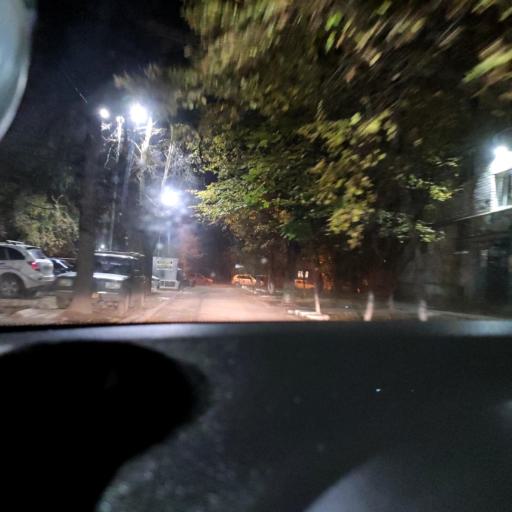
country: RU
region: Samara
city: Petra-Dubrava
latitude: 53.2302
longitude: 50.2755
